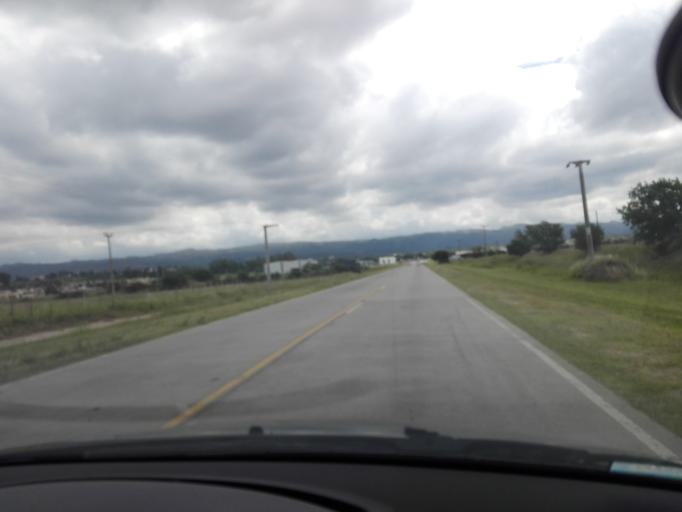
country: AR
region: Cordoba
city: Alta Gracia
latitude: -31.6347
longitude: -64.4256
